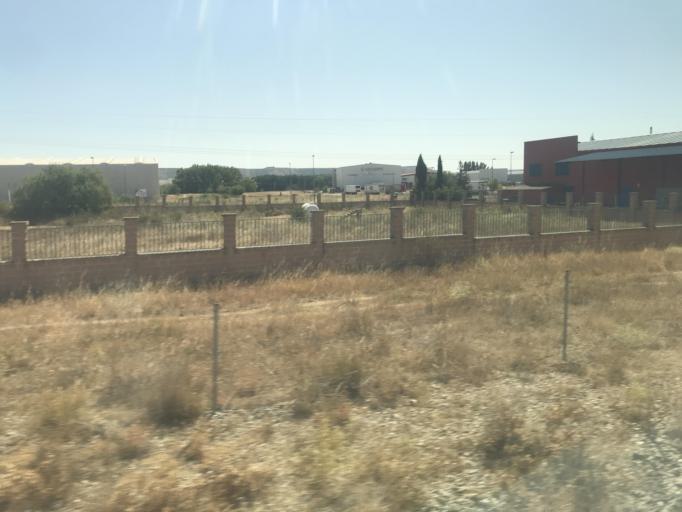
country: ES
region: Castille and Leon
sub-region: Provincia de Palencia
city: Duenas
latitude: 41.8495
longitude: -4.5543
